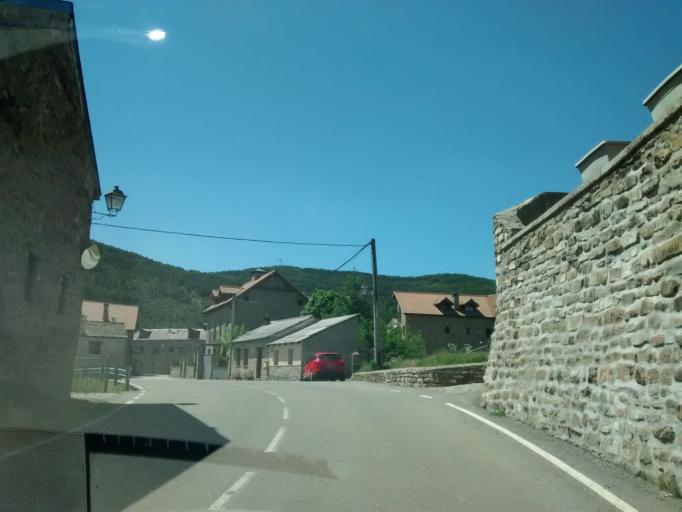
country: ES
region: Aragon
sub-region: Provincia de Huesca
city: Borau
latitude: 42.6570
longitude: -0.5640
